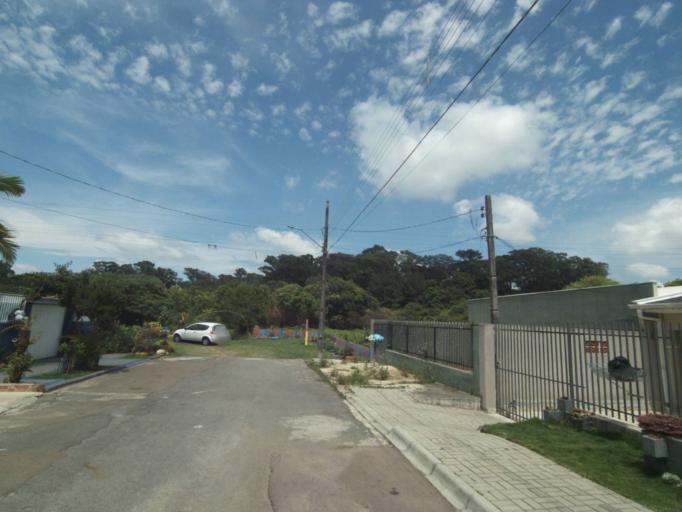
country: BR
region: Parana
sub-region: Curitiba
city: Curitiba
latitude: -25.4594
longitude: -49.3536
